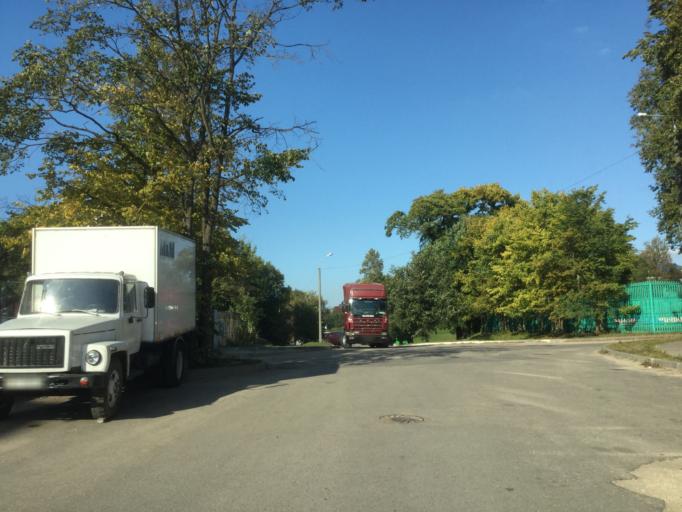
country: BY
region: Vitebsk
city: Vitebsk
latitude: 55.1730
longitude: 30.1952
